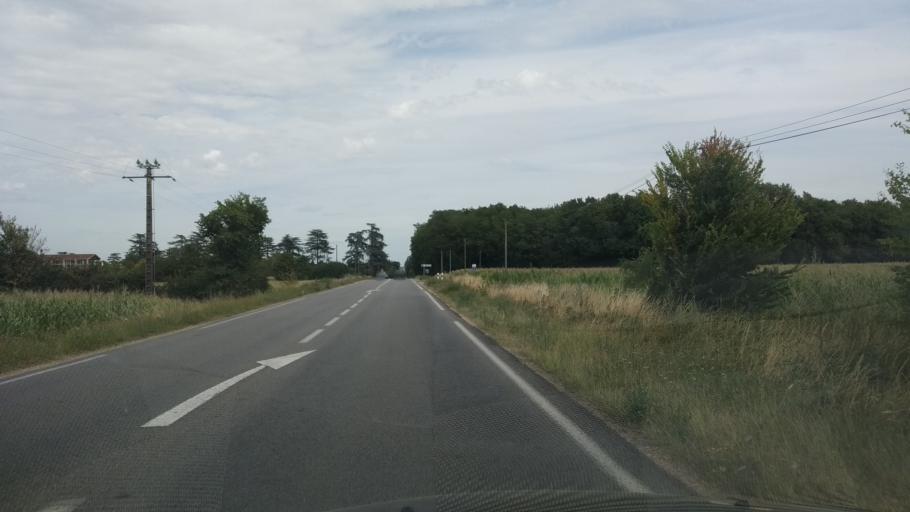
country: FR
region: Poitou-Charentes
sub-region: Departement de la Vienne
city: Mignaloux-Beauvoir
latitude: 46.5627
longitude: 0.4171
